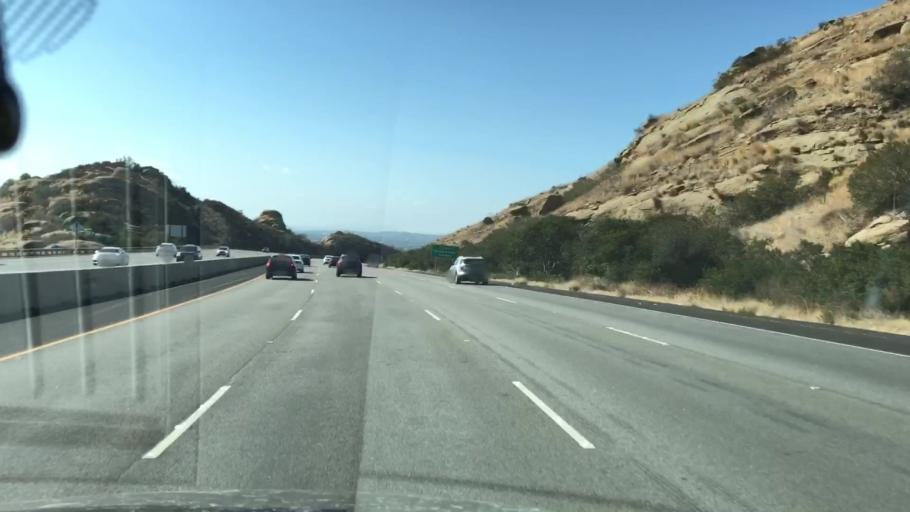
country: US
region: California
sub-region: Los Angeles County
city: Chatsworth
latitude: 34.2703
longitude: -118.6492
